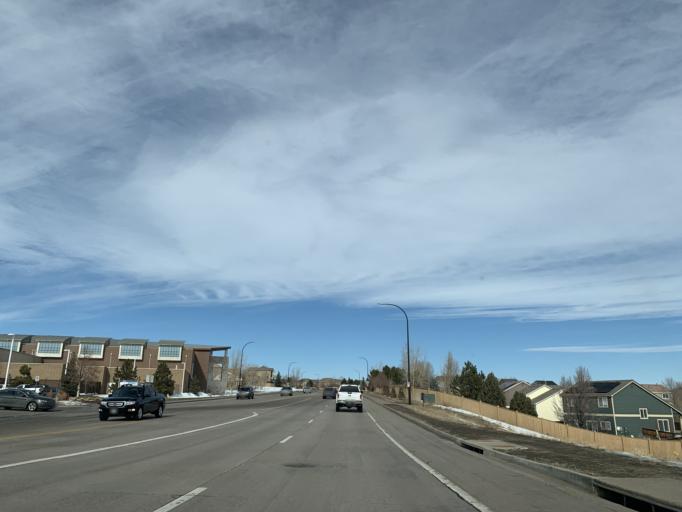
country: US
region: Colorado
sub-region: Douglas County
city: Carriage Club
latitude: 39.5231
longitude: -104.9324
